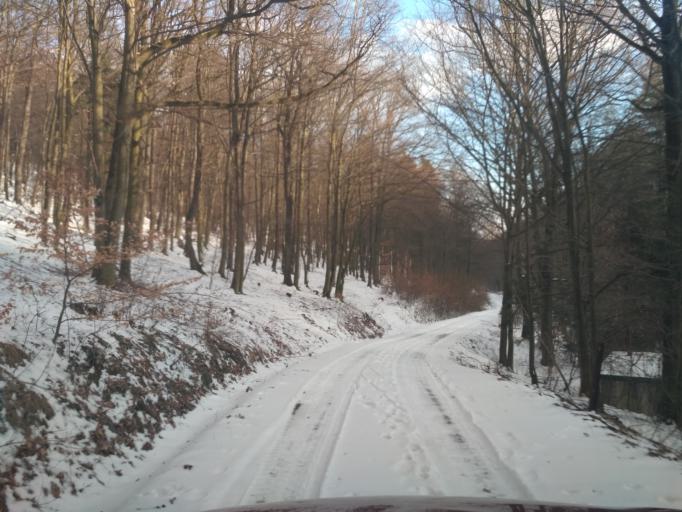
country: SK
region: Kosicky
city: Kosice
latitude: 48.7457
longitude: 21.1519
